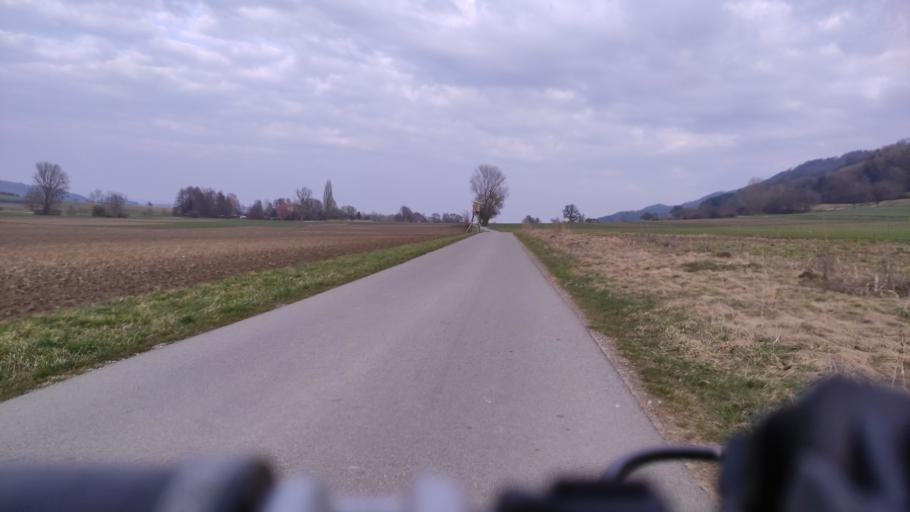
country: DE
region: Baden-Wuerttemberg
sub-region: Freiburg Region
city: Rielasingen-Worblingen
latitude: 47.7108
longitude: 8.8418
